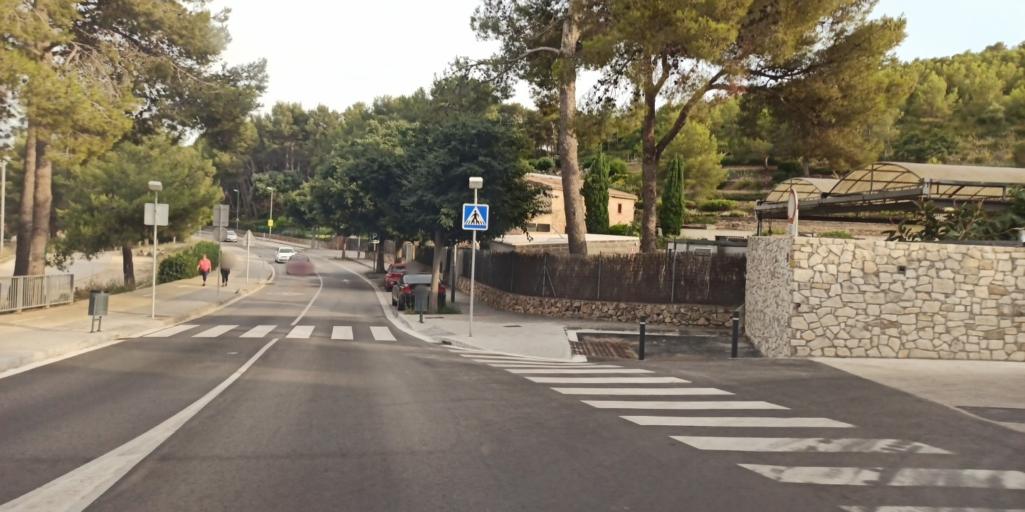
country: ES
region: Catalonia
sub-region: Provincia de Barcelona
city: Castelldefels
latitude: 41.2886
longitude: 1.9720
